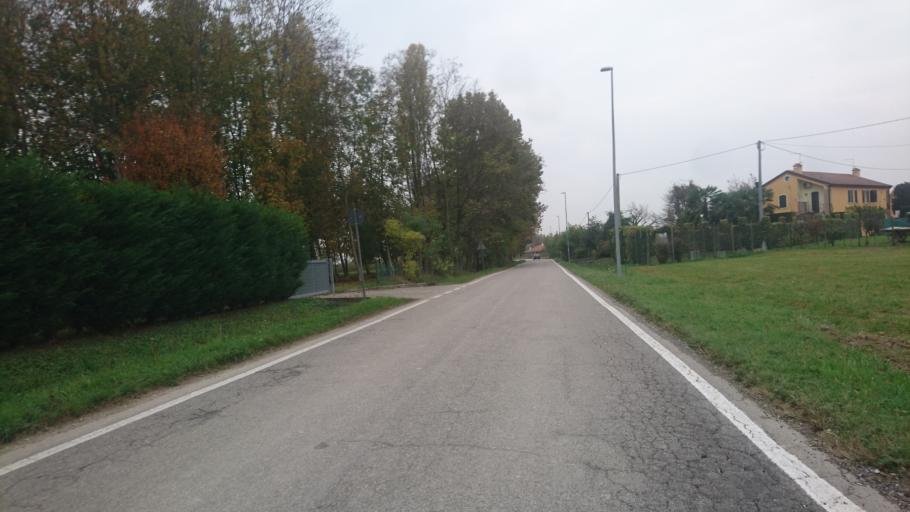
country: IT
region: Veneto
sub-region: Provincia di Venezia
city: Tombelle
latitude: 45.3861
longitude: 11.9826
